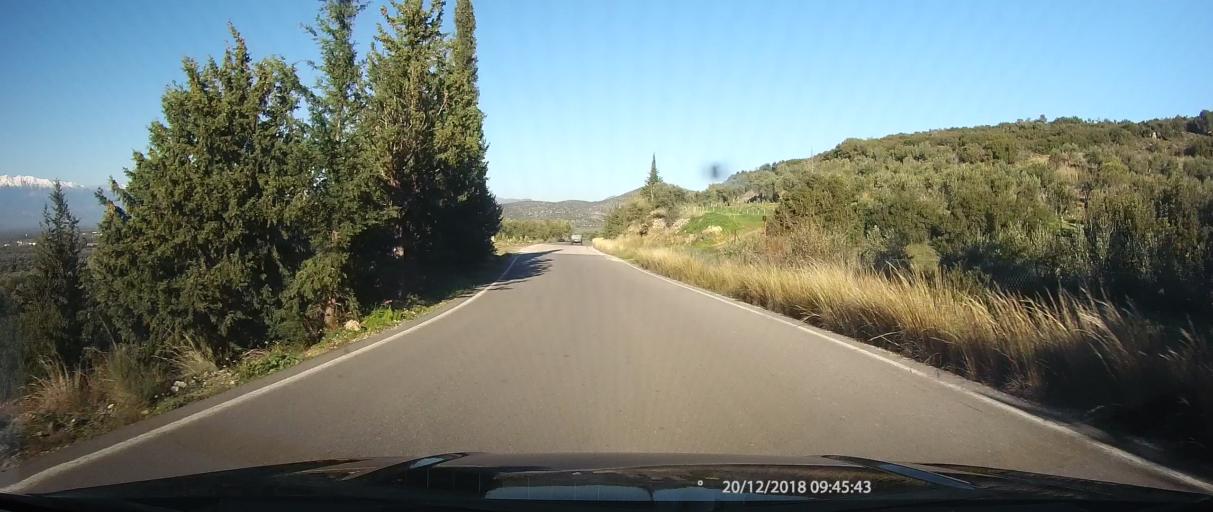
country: GR
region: Peloponnese
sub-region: Nomos Lakonias
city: Yerakion
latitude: 36.9858
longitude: 22.7234
